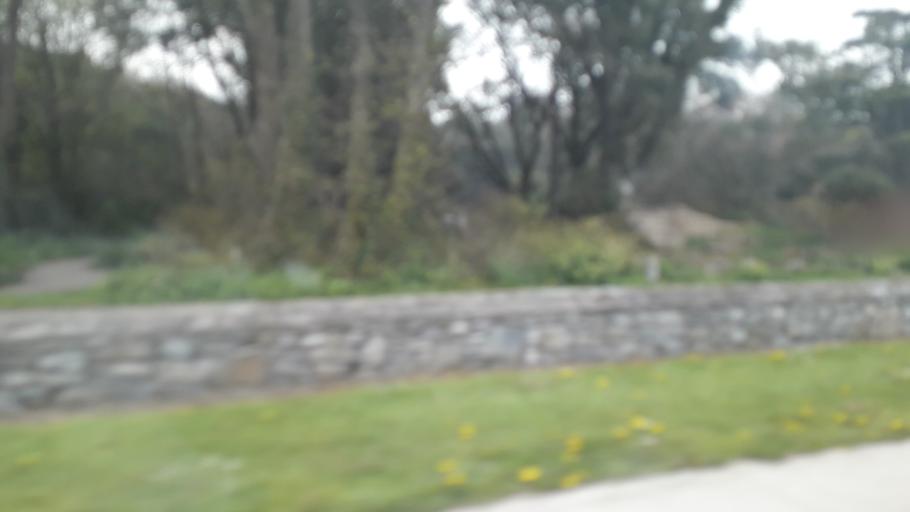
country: IE
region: Leinster
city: Dollymount
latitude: 53.3709
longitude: -6.1673
